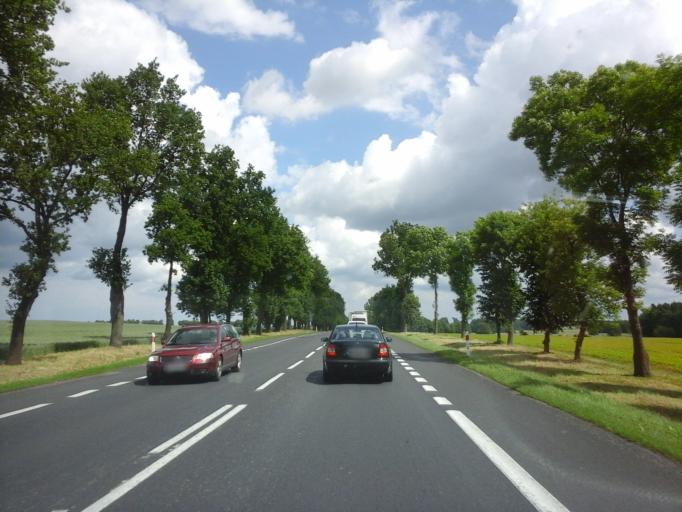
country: PL
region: West Pomeranian Voivodeship
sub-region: Powiat bialogardzki
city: Bialogard
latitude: 54.1121
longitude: 16.0017
